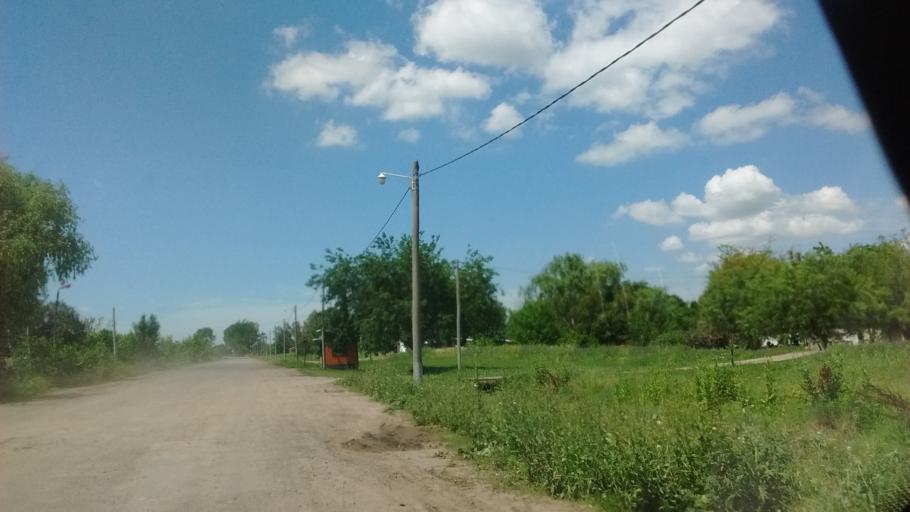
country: AR
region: Santa Fe
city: Funes
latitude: -32.8480
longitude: -60.7960
